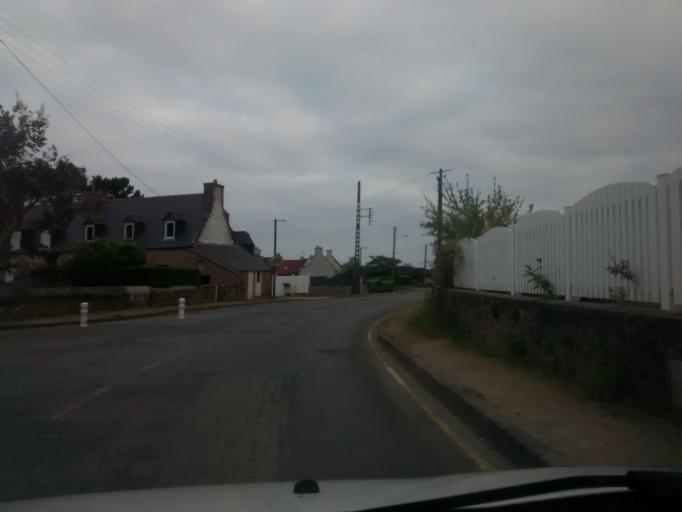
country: FR
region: Brittany
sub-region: Departement des Cotes-d'Armor
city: Tregastel
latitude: 48.8202
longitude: -3.4760
